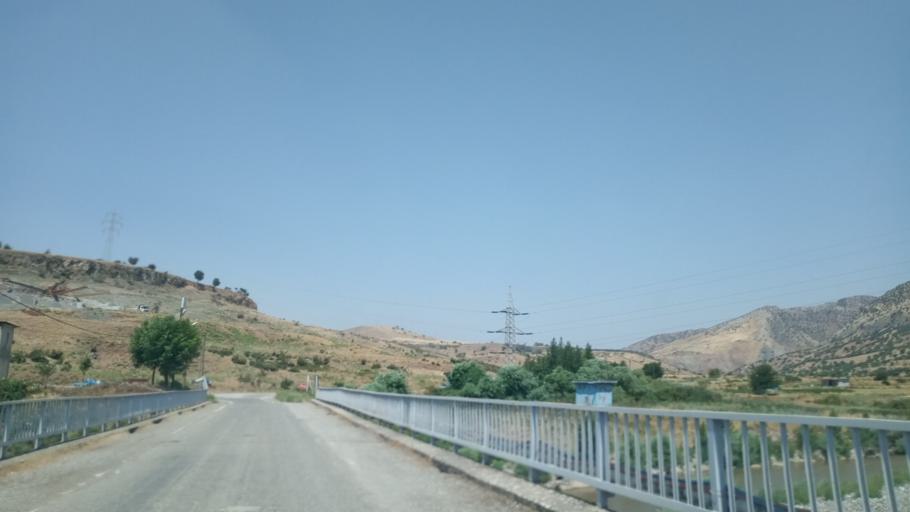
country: TR
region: Siirt
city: Dilektepe
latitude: 38.0605
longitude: 41.7799
